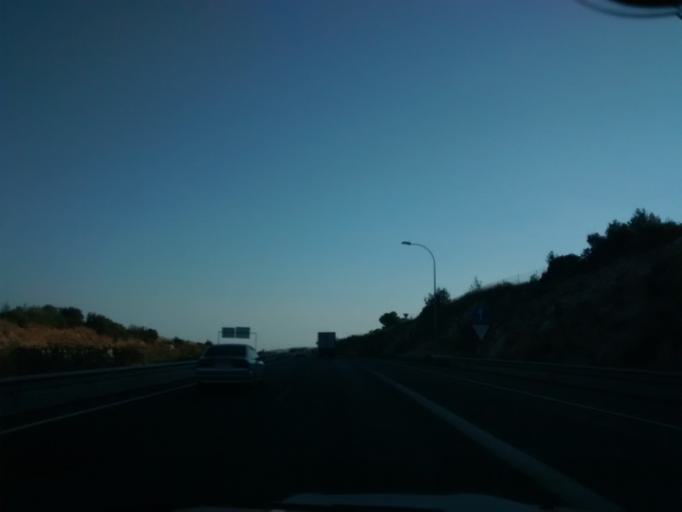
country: ES
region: Balearic Islands
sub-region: Illes Balears
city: Inca
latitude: 39.7331
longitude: 2.9372
